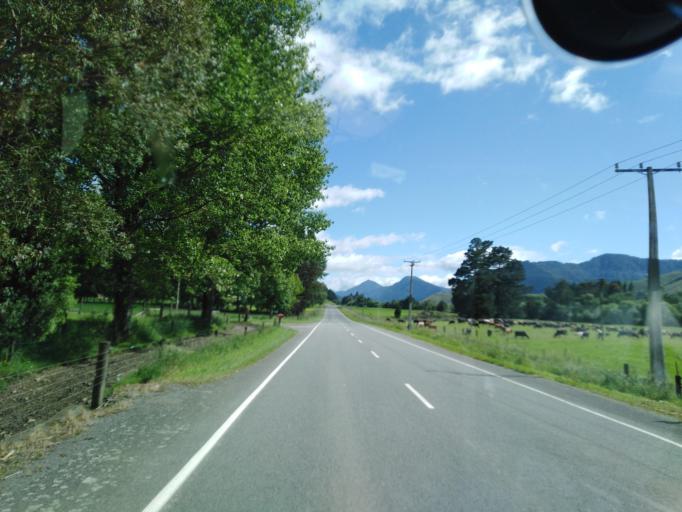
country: NZ
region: Nelson
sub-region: Nelson City
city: Nelson
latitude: -41.2667
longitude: 173.5727
